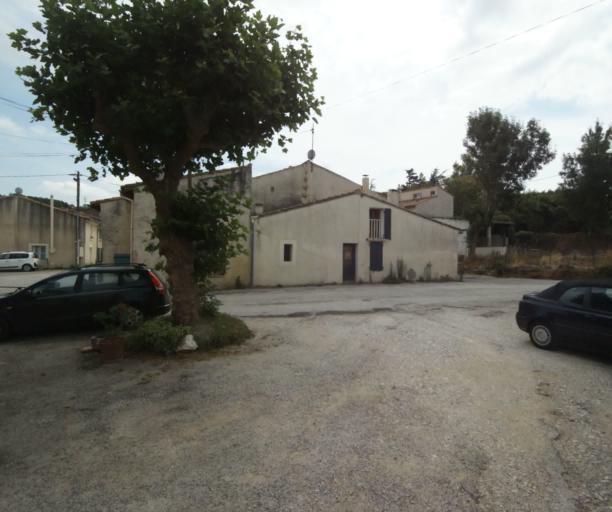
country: FR
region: Midi-Pyrenees
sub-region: Departement de la Haute-Garonne
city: Revel
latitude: 43.4496
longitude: 2.0348
